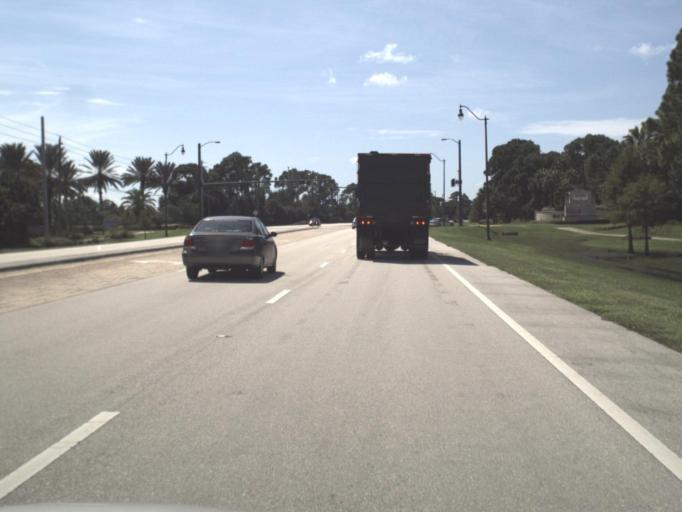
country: US
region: Florida
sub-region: Sarasota County
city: North Port
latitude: 27.0537
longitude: -82.1572
